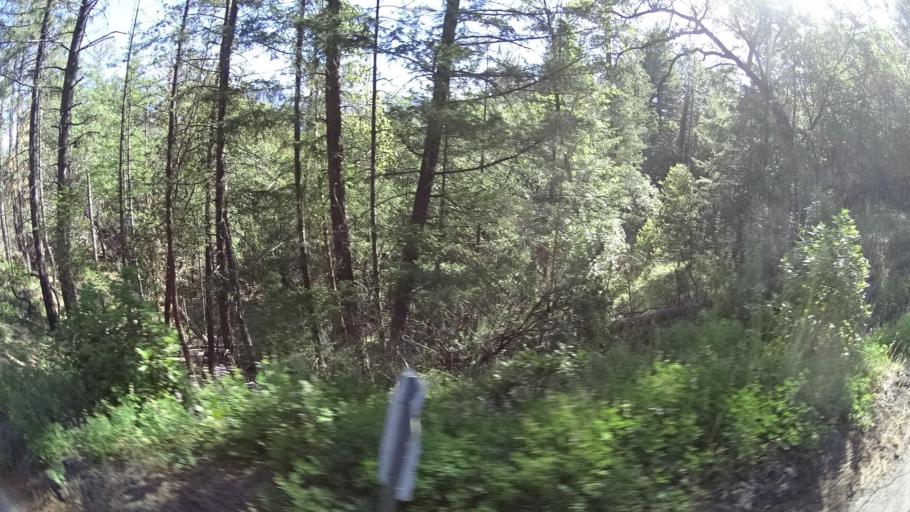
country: US
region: California
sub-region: Lake County
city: Upper Lake
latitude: 39.4011
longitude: -122.9584
